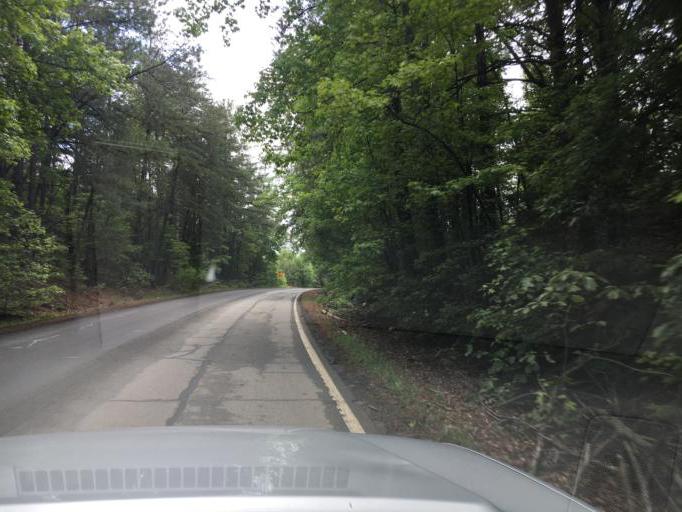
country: US
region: South Carolina
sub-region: Greenville County
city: Five Forks
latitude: 34.8489
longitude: -82.2777
